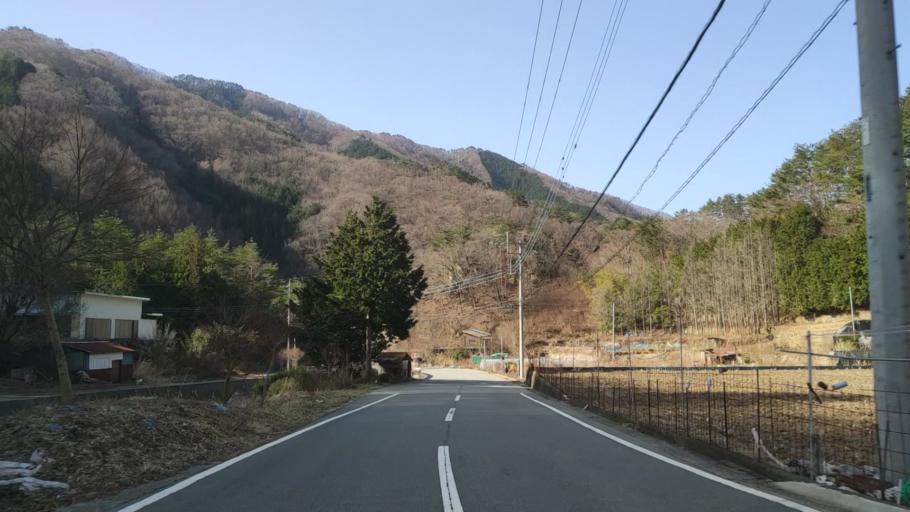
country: JP
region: Yamanashi
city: Fujikawaguchiko
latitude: 35.5512
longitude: 138.6606
